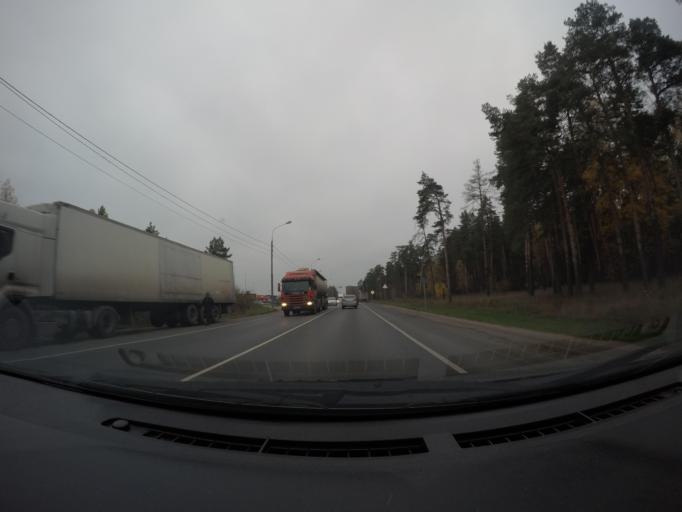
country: RU
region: Moskovskaya
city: Malyshevo
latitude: 55.4635
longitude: 38.3343
